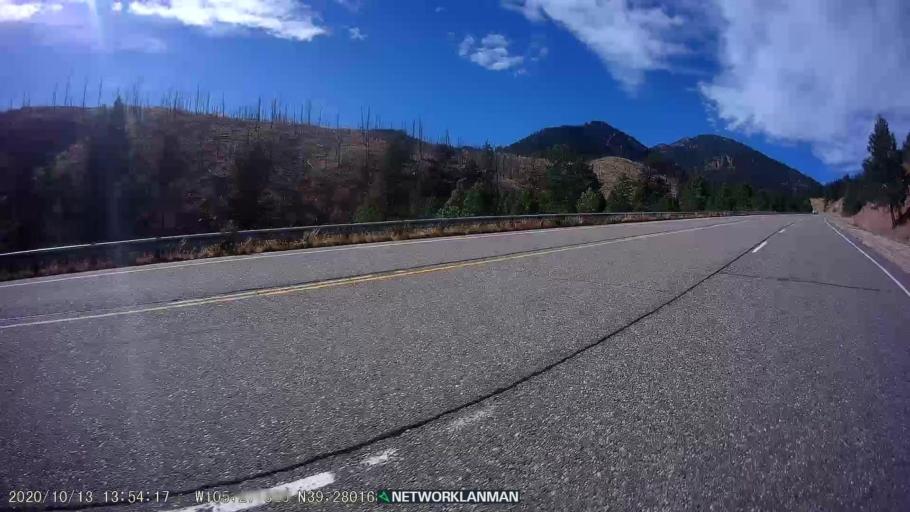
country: US
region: Colorado
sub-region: Douglas County
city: Roxborough Park
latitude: 39.2801
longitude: -105.2735
